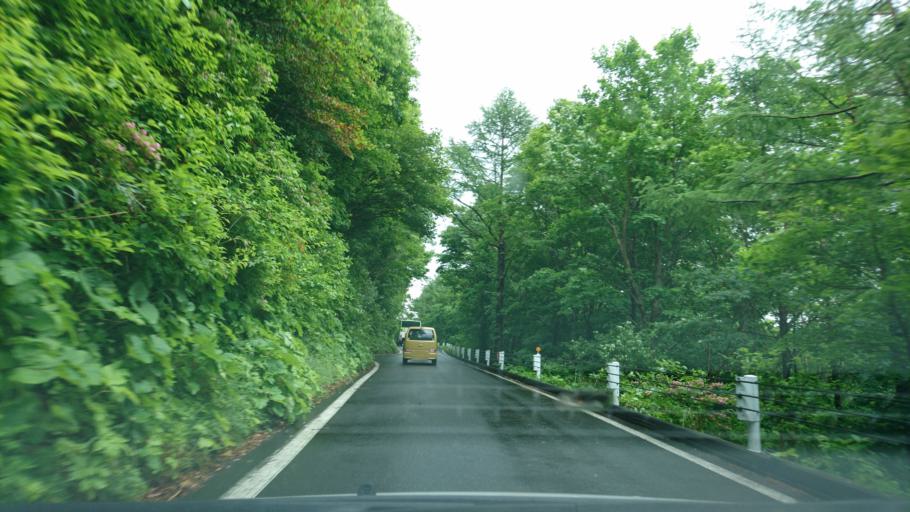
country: JP
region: Iwate
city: Ichinoseki
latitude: 38.9956
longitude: 140.8234
